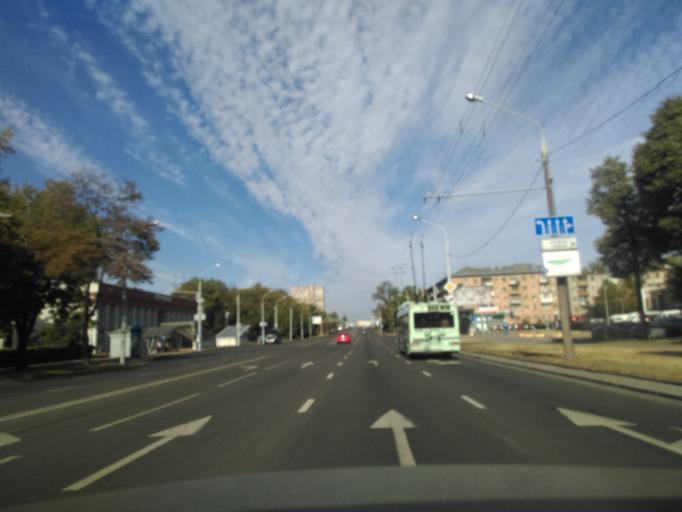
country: BY
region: Minsk
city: Minsk
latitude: 53.8830
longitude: 27.5939
